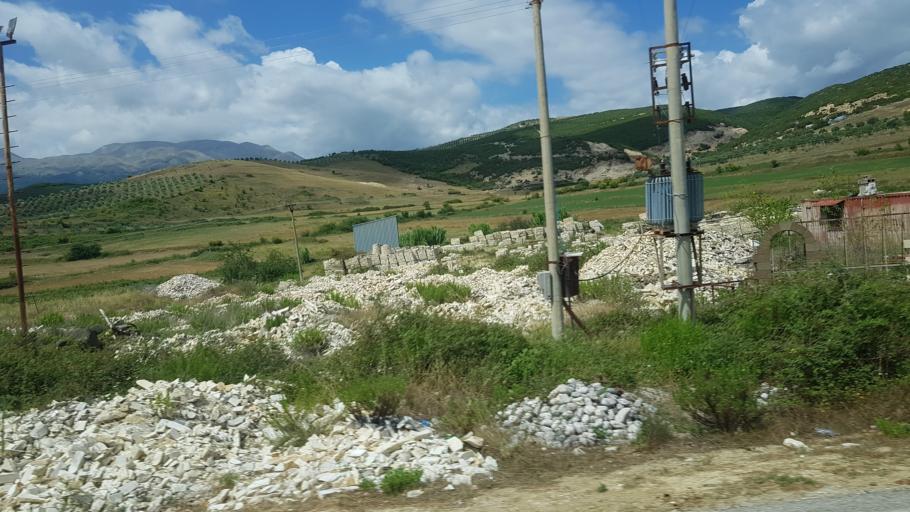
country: AL
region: Gjirokaster
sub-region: Rrethi i Tepelenes
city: Krahes
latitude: 40.4264
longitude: 19.8540
